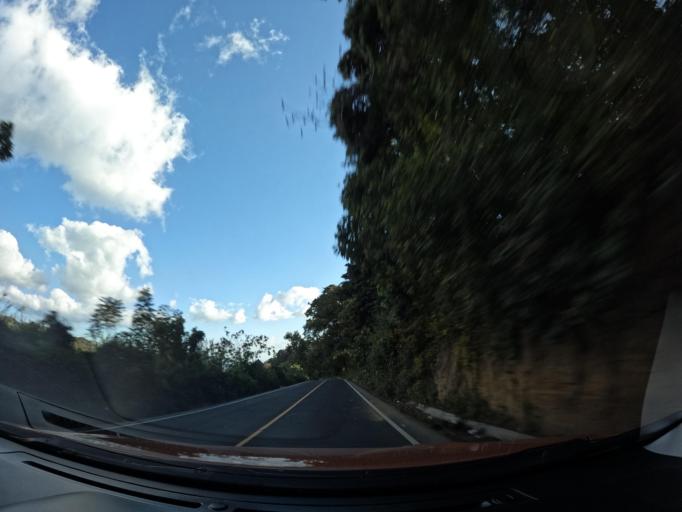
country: GT
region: Sacatepequez
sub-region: Municipio de Santa Maria de Jesus
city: Santa Maria de Jesus
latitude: 14.4756
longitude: -90.6943
